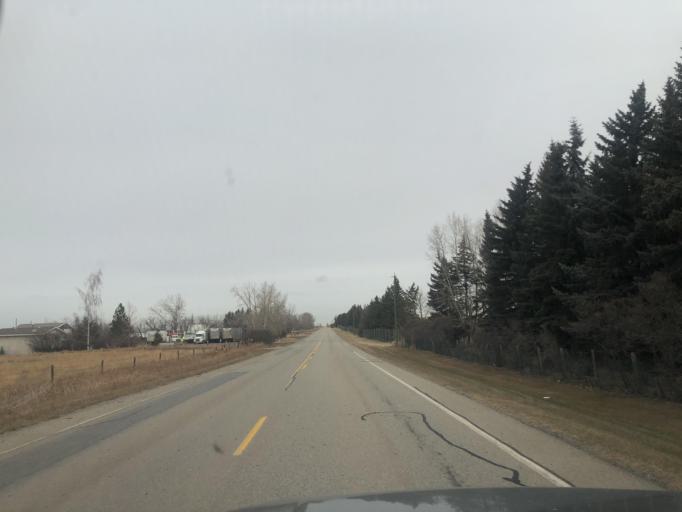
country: CA
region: Alberta
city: Chestermere
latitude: 50.9934
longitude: -113.8654
